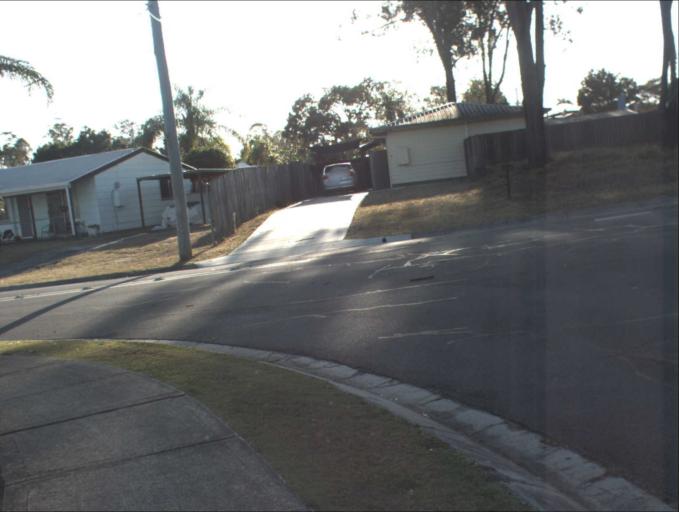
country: AU
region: Queensland
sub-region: Gold Coast
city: Yatala
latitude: -27.7078
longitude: 153.2142
